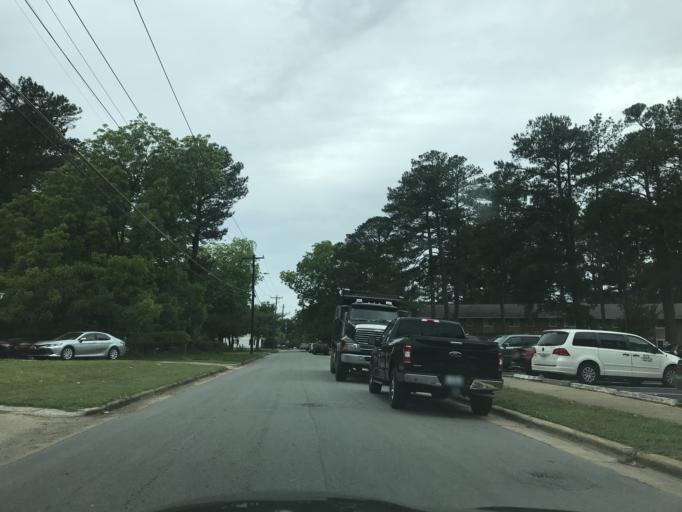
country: US
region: North Carolina
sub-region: Wake County
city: West Raleigh
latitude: 35.7918
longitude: -78.6920
